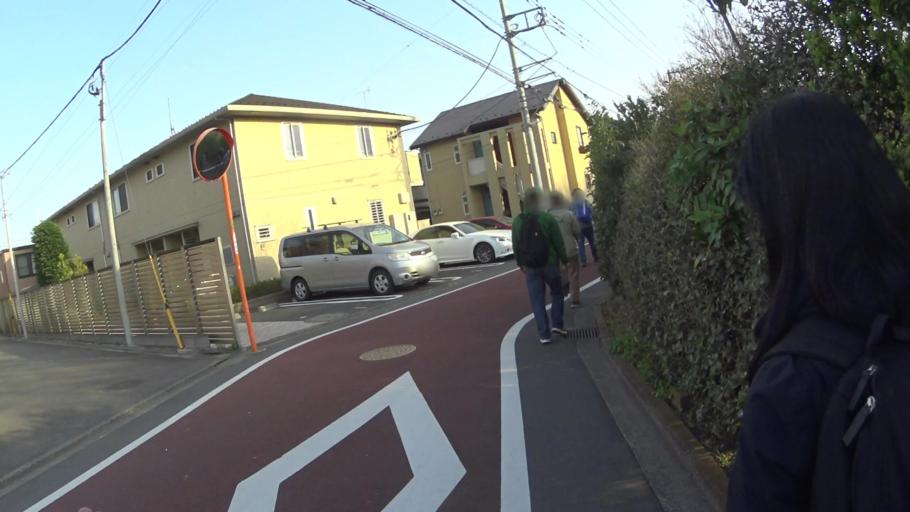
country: JP
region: Tokyo
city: Kokubunji
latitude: 35.7053
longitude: 139.5027
